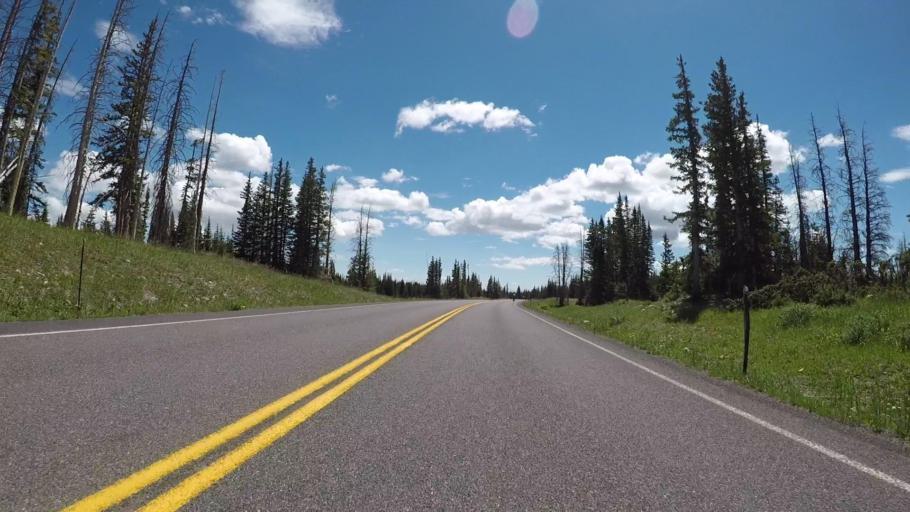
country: US
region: Wyoming
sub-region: Carbon County
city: Saratoga
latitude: 41.3520
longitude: -106.2620
